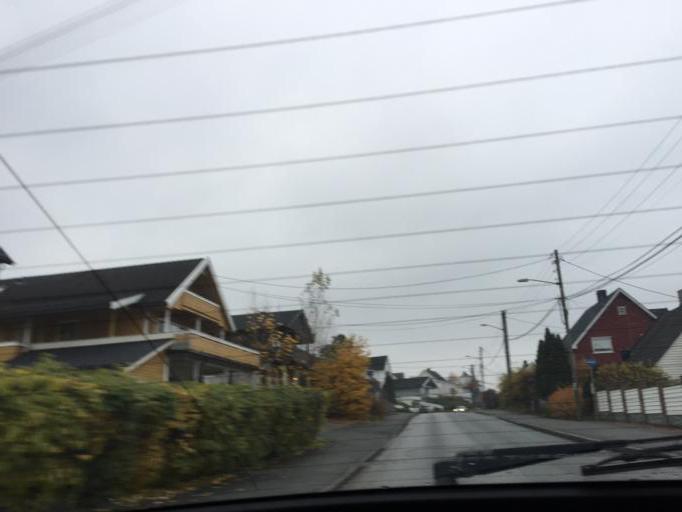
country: NO
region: Buskerud
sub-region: Drammen
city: Drammen
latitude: 59.7303
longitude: 10.2019
